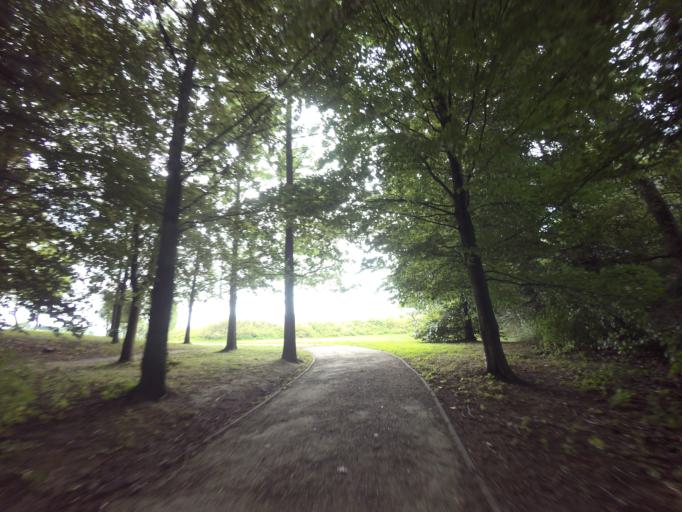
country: BE
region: Flanders
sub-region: Provincie Vlaams-Brabant
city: Grimbergen
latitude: 50.9141
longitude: 4.3613
